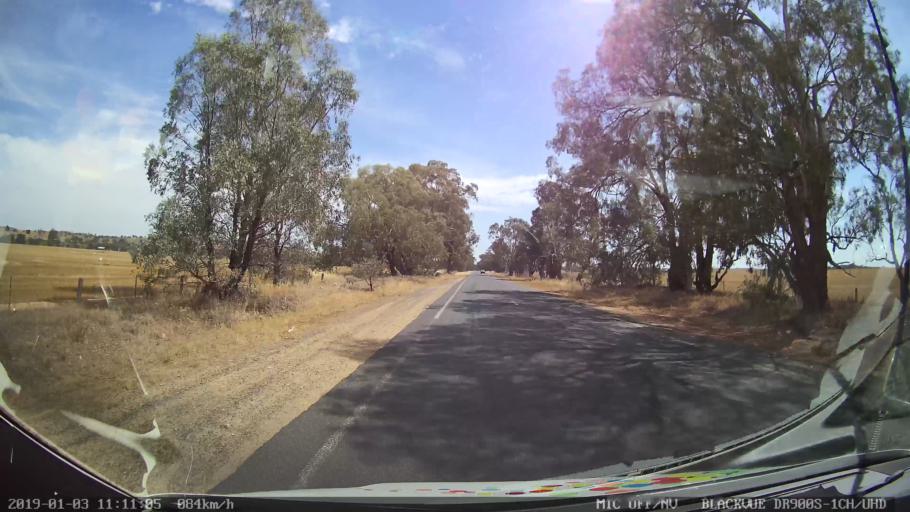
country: AU
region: New South Wales
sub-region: Young
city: Young
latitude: -34.2192
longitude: 148.2592
